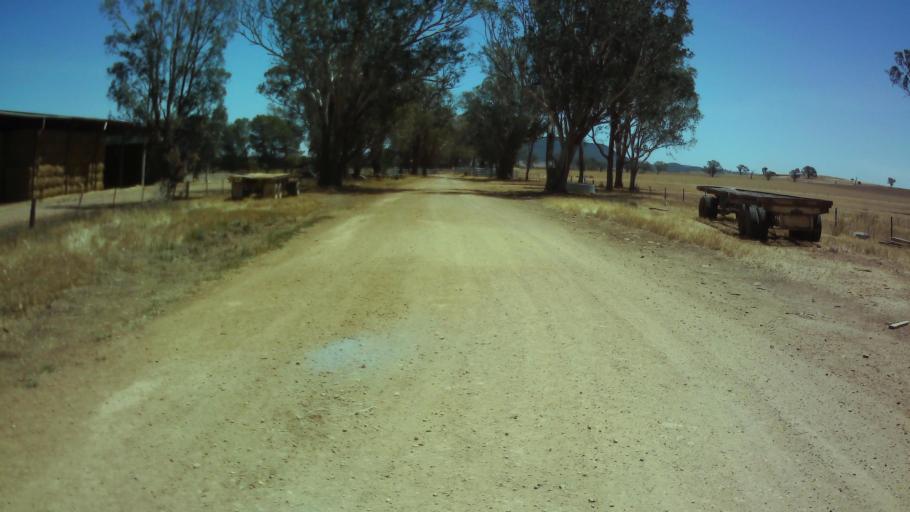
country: AU
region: New South Wales
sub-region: Weddin
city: Grenfell
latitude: -34.0110
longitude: 148.1703
